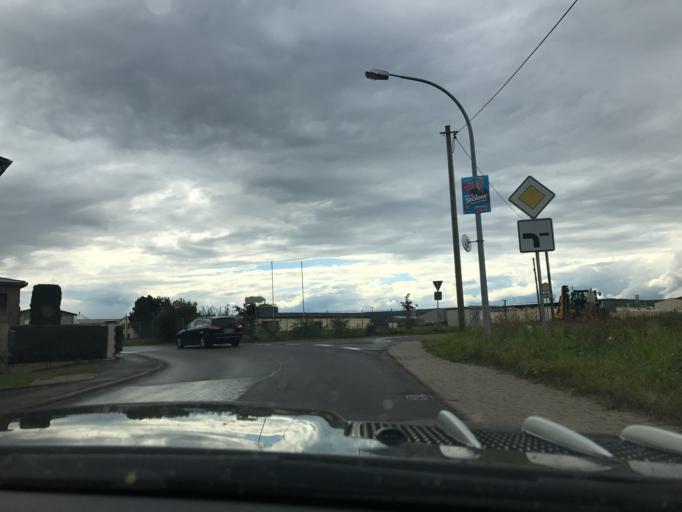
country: DE
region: Thuringia
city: Niederdorla
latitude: 51.1577
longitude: 10.4402
